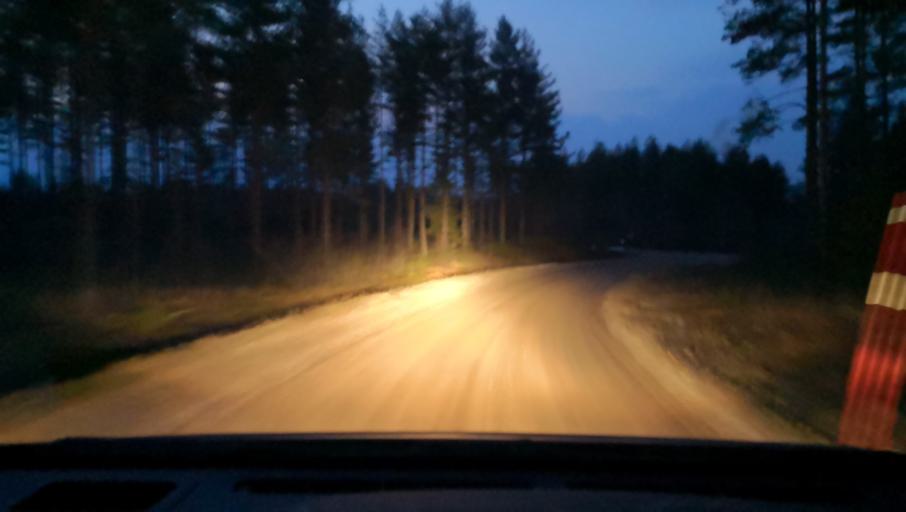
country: SE
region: OErebro
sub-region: Lindesbergs Kommun
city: Frovi
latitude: 59.6082
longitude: 15.4770
